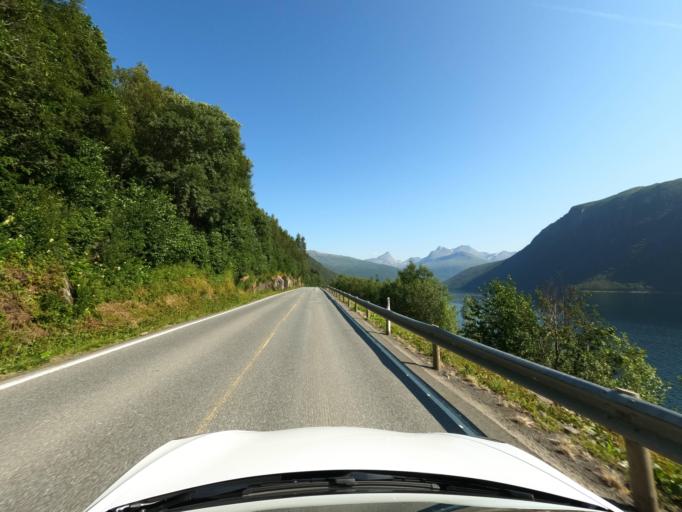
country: NO
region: Nordland
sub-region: Narvik
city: Narvik
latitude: 68.3963
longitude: 17.5154
